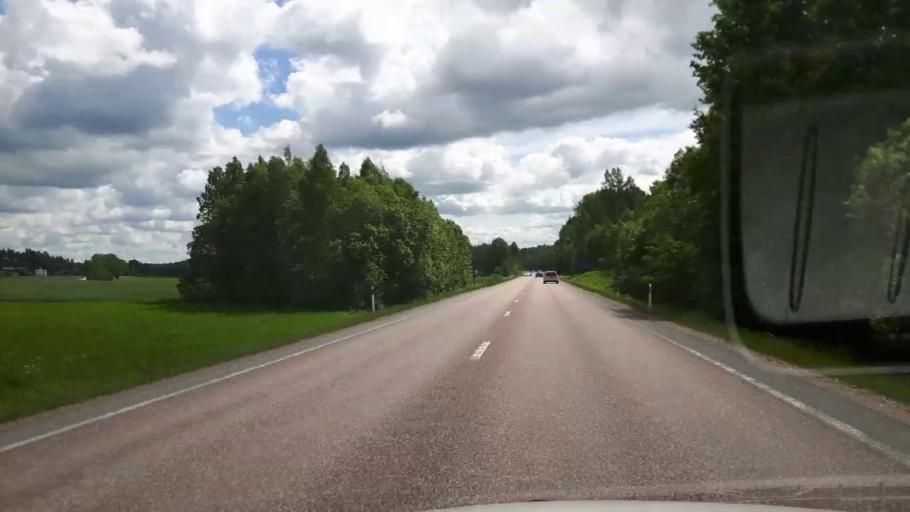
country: SE
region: Dalarna
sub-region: Saters Kommun
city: Saeter
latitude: 60.4805
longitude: 15.7763
